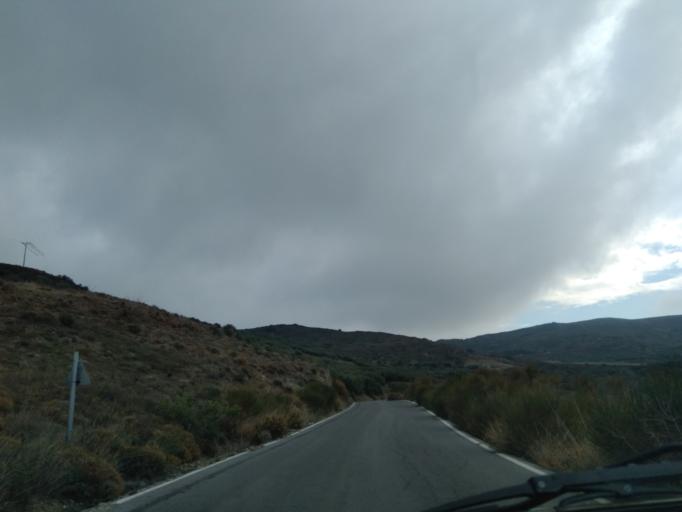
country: GR
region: Crete
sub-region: Nomos Lasithiou
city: Siteia
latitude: 35.1407
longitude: 26.0220
